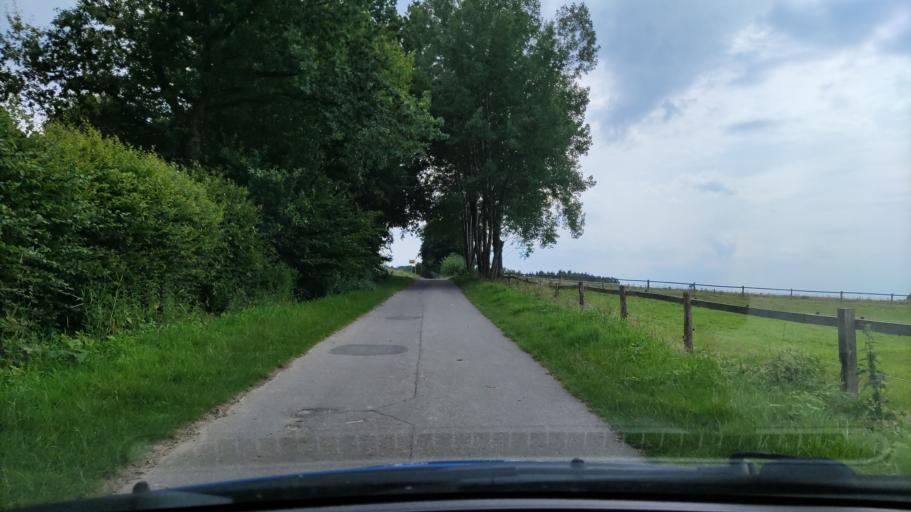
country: DE
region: Lower Saxony
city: Hanstedt
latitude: 53.2349
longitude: 10.0277
